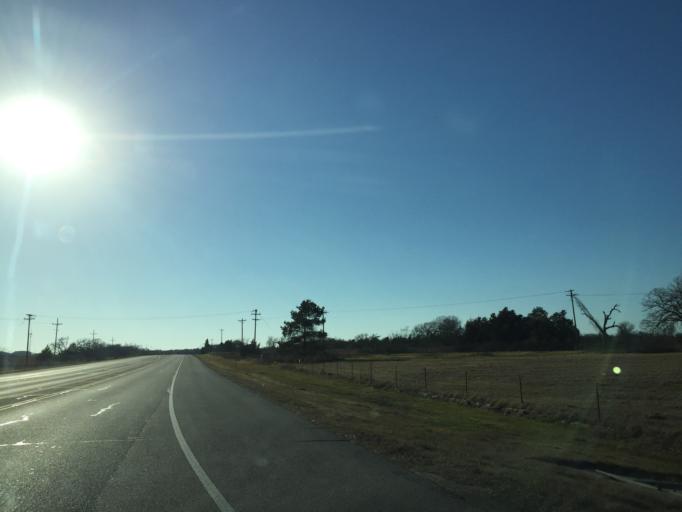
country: US
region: Texas
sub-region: Bastrop County
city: Elgin
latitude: 30.3801
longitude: -97.2442
